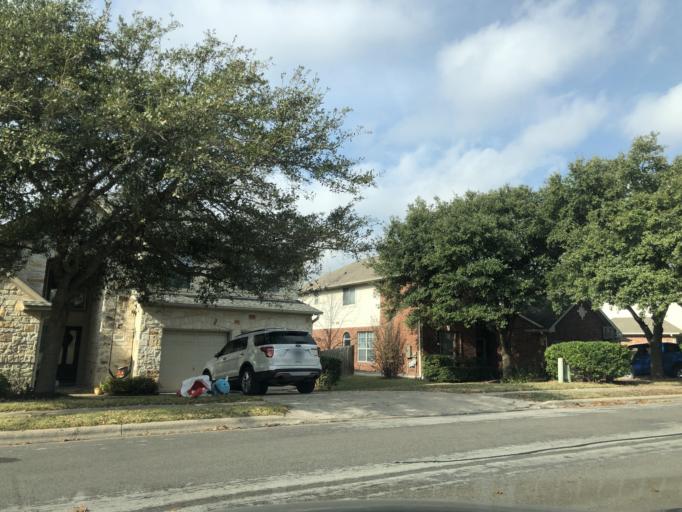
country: US
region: Texas
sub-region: Travis County
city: Wells Branch
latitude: 30.4229
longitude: -97.6829
